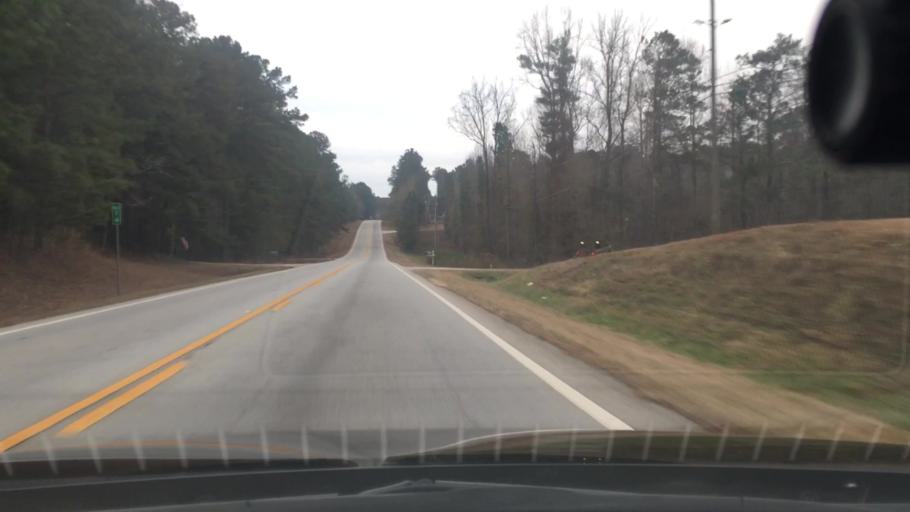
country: US
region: Georgia
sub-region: Fayette County
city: Peachtree City
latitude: 33.3812
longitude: -84.6259
